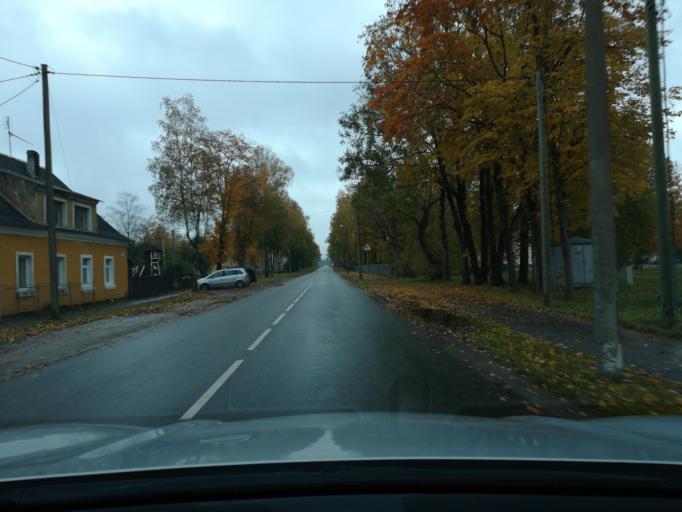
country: EE
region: Ida-Virumaa
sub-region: Johvi vald
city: Johvi
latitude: 59.3116
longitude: 27.4530
